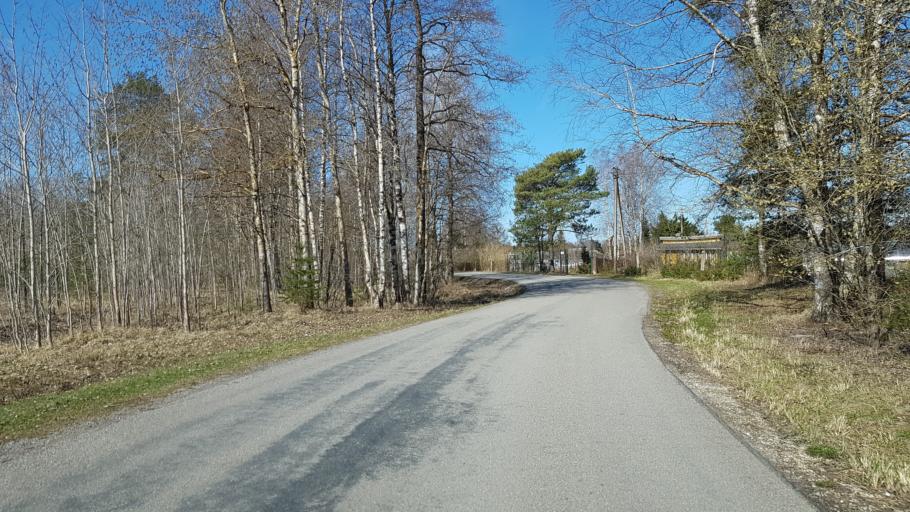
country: EE
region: Ida-Virumaa
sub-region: Narva-Joesuu linn
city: Narva-Joesuu
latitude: 59.4129
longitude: 28.0672
